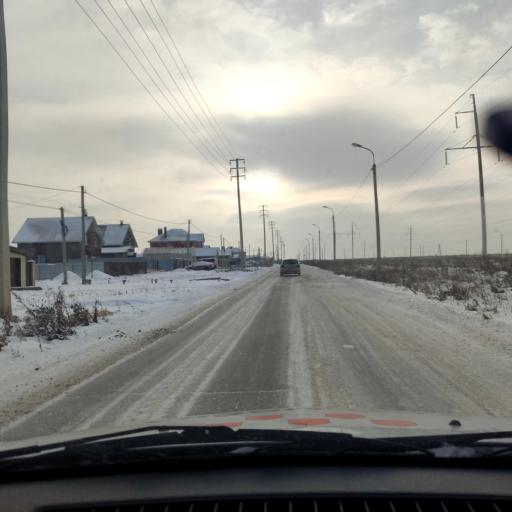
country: RU
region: Bashkortostan
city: Kabakovo
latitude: 54.6160
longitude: 56.0895
